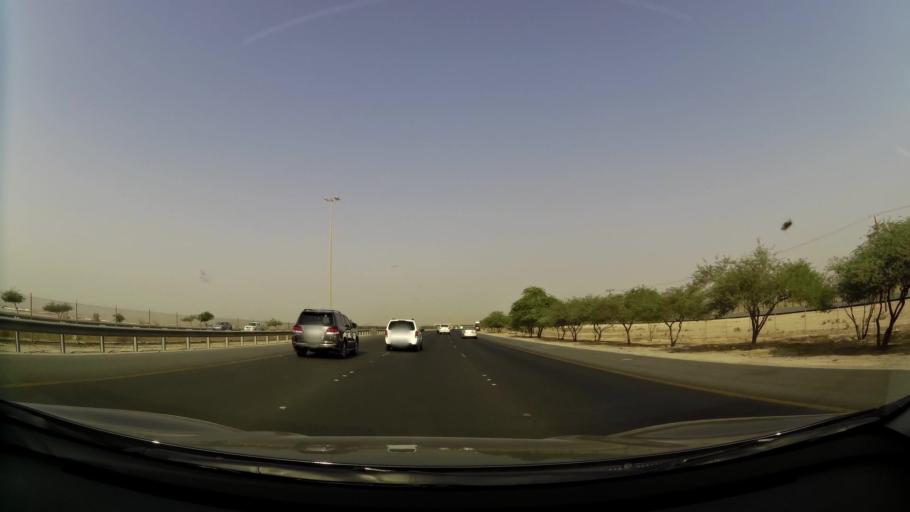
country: KW
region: Mubarak al Kabir
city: Mubarak al Kabir
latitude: 29.1760
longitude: 48.0354
